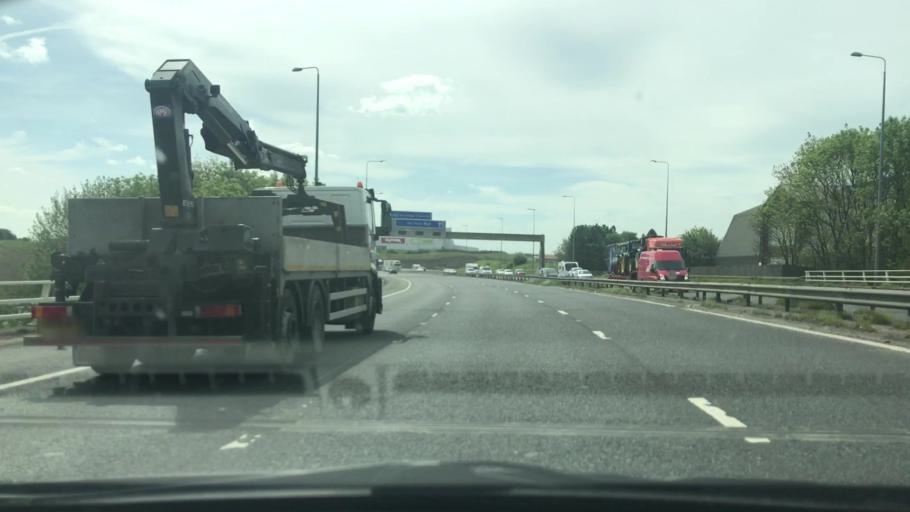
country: GB
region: England
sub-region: City and Borough of Wakefield
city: Ferrybridge
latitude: 53.7012
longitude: -1.2777
